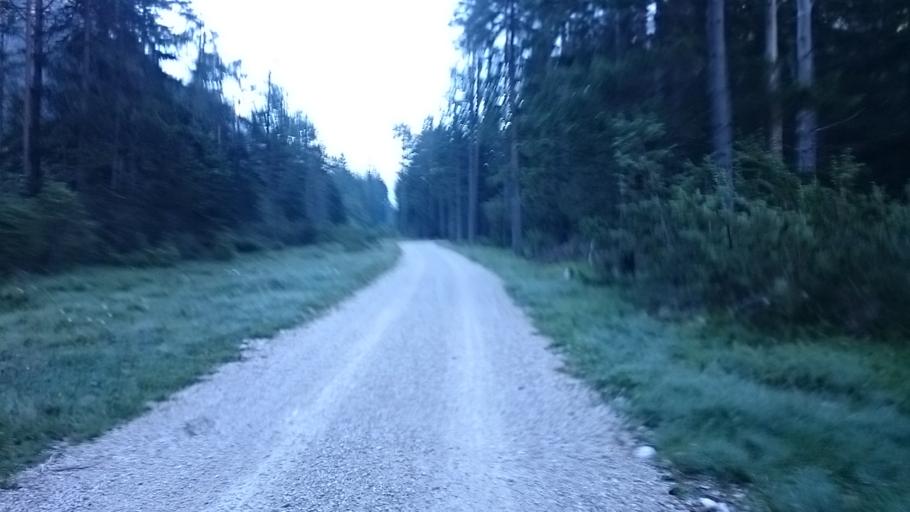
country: IT
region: Trentino-Alto Adige
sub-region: Bolzano
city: Dobbiaco
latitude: 46.6667
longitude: 12.2240
